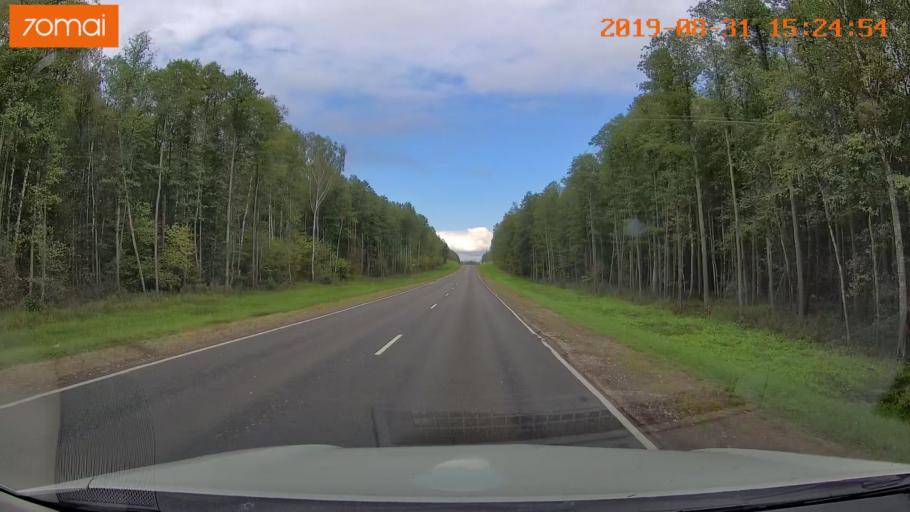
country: RU
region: Kaluga
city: Baryatino
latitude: 54.5340
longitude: 34.5116
